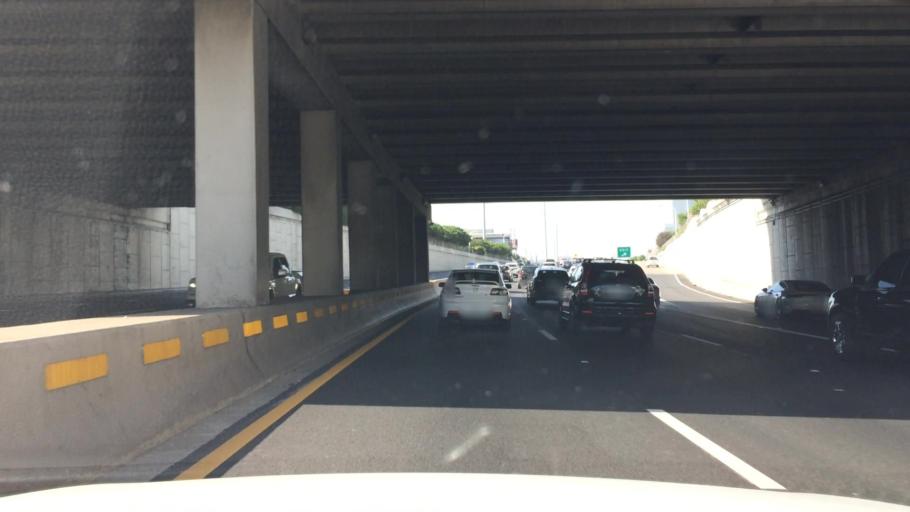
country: US
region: Texas
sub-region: Dallas County
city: Addison
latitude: 32.9598
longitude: -96.8211
